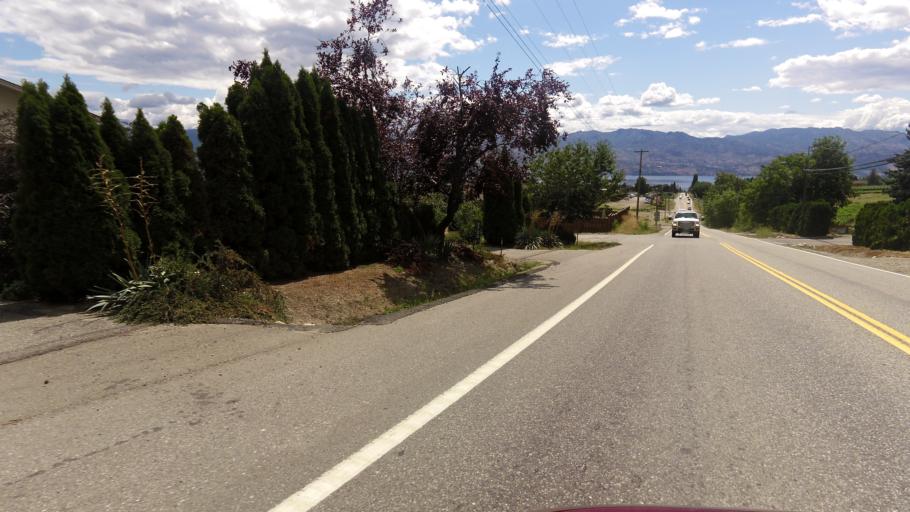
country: CA
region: British Columbia
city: West Kelowna
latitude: 49.8592
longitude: -119.5555
